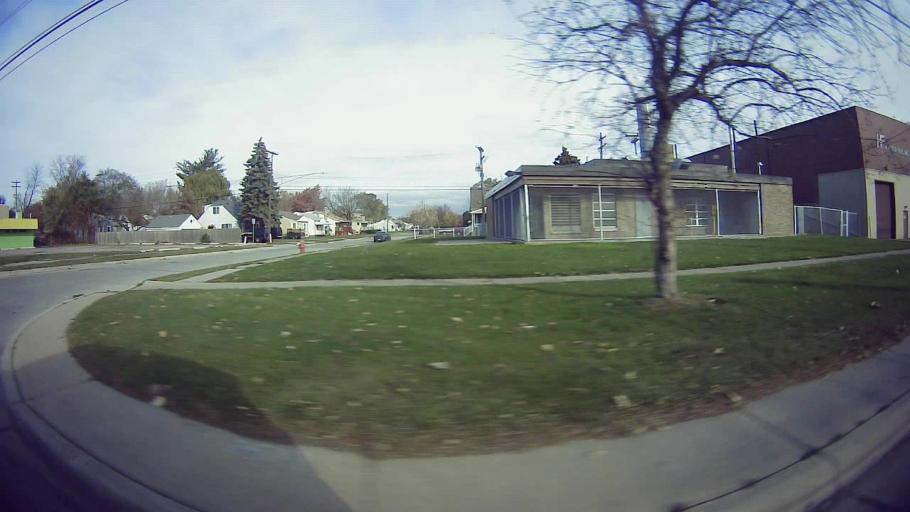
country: US
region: Michigan
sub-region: Macomb County
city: Eastpointe
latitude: 42.4645
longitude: -82.9718
